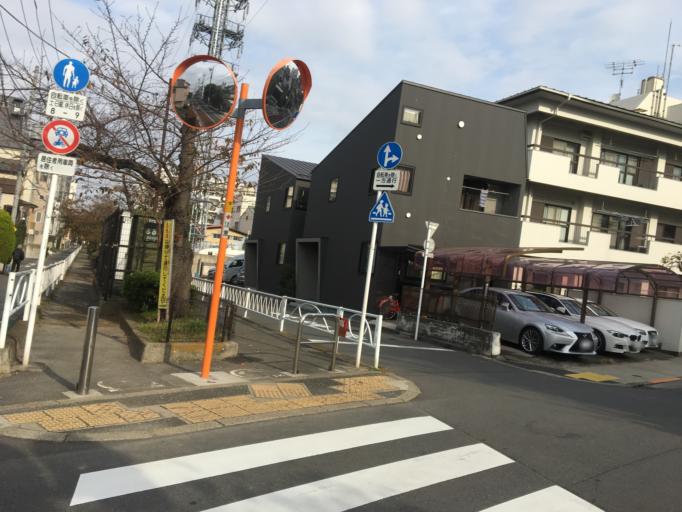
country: JP
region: Tokyo
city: Tokyo
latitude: 35.6111
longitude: 139.6796
